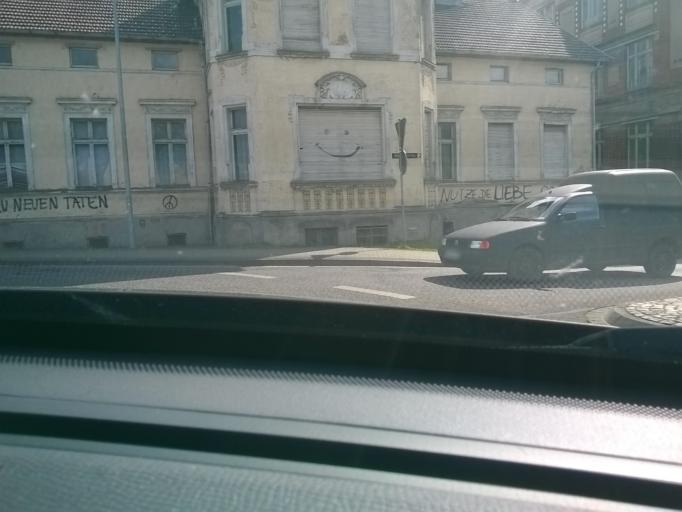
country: DE
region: Brandenburg
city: Wittstock
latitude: 53.1638
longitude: 12.4923
